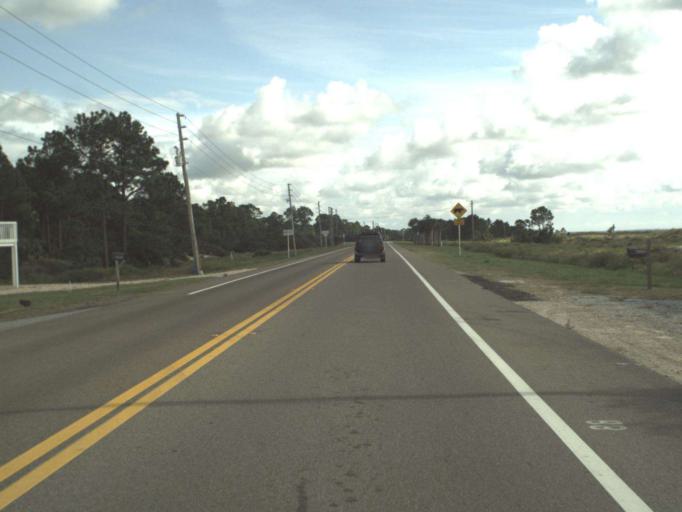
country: US
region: Florida
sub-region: Bay County
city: Mexico Beach
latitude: 29.8938
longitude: -85.3593
